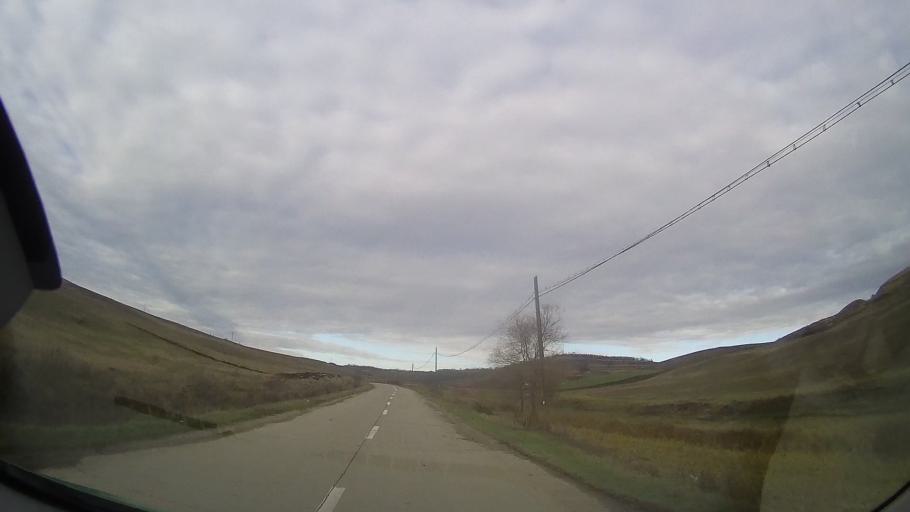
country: RO
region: Bistrita-Nasaud
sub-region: Comuna Micestii de Campie
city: Micestii de Campie
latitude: 46.8409
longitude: 24.3029
